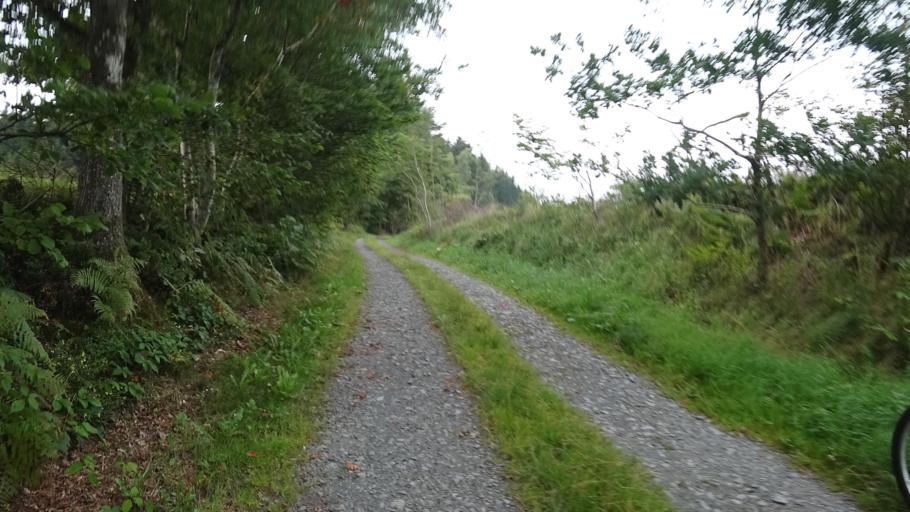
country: BE
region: Wallonia
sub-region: Province du Luxembourg
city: Chiny
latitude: 49.7987
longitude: 5.3311
